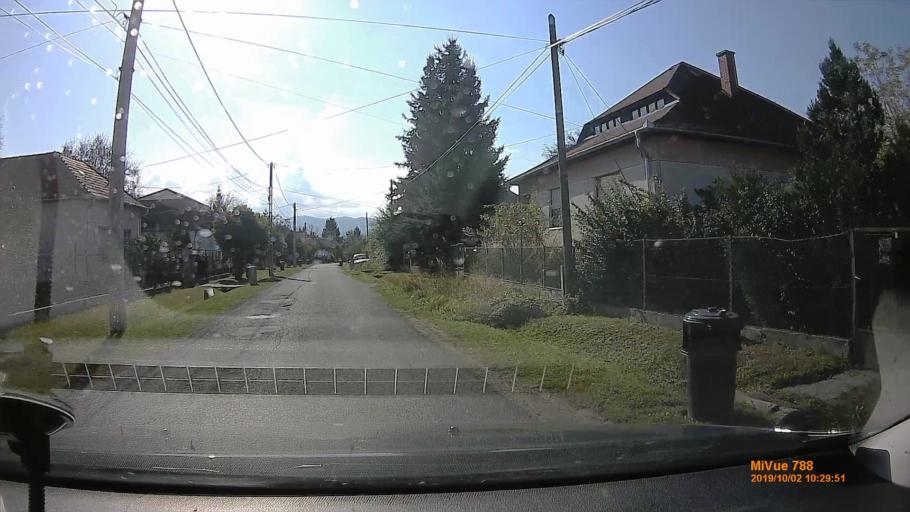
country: HU
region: Nograd
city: Kazar
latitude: 48.0200
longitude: 19.8254
